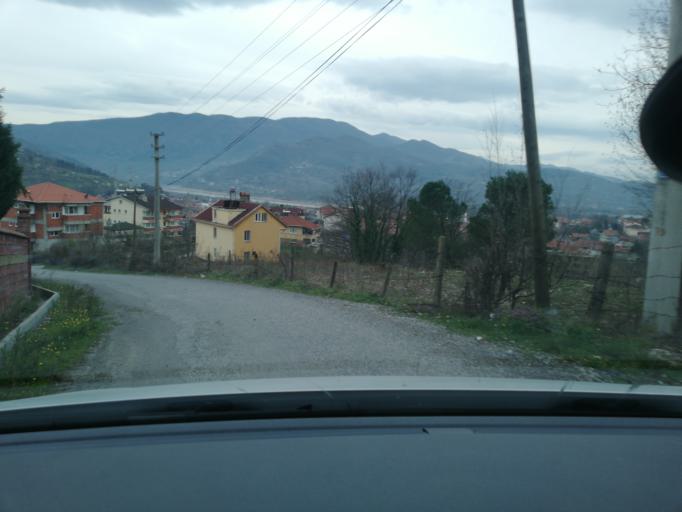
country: TR
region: Zonguldak
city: Gokcebey
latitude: 41.3114
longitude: 32.1431
